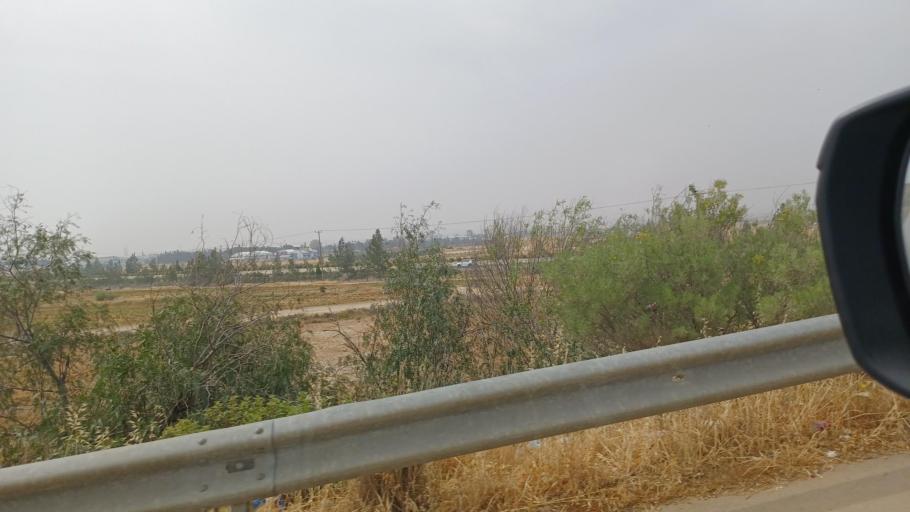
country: CY
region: Lefkosia
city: Kokkinotrimithia
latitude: 35.1606
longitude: 33.2208
